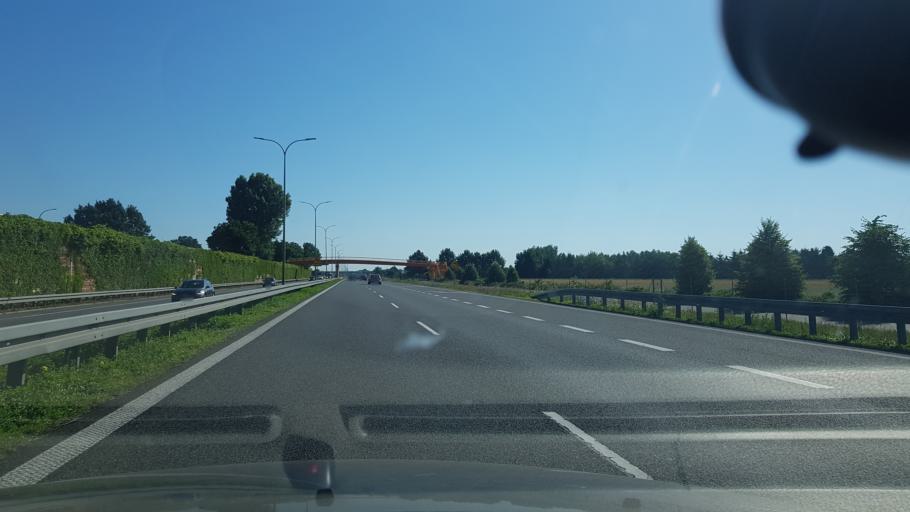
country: PL
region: Masovian Voivodeship
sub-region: Powiat wolominski
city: Dabrowka
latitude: 52.4745
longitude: 21.3322
